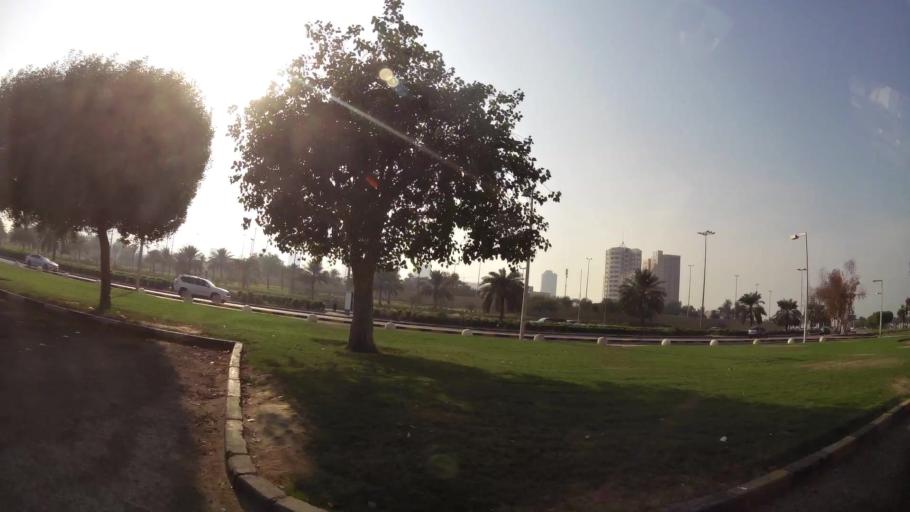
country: KW
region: Al Asimah
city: Ad Dasmah
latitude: 29.3884
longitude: 48.0024
